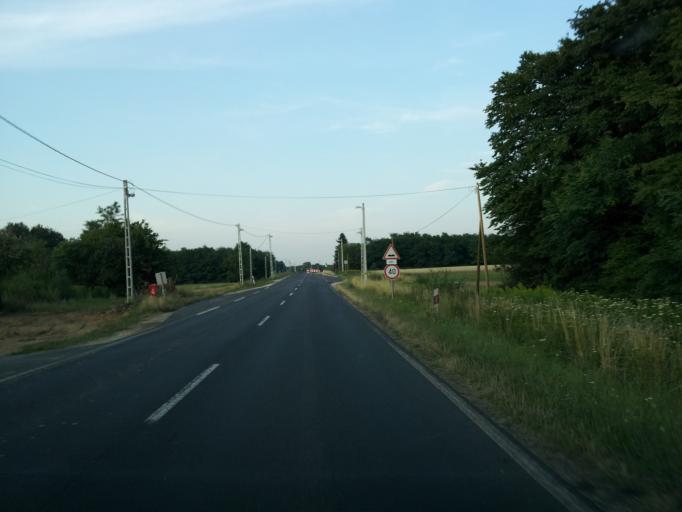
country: HU
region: Zala
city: Zalalovo
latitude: 46.8127
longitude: 16.5684
